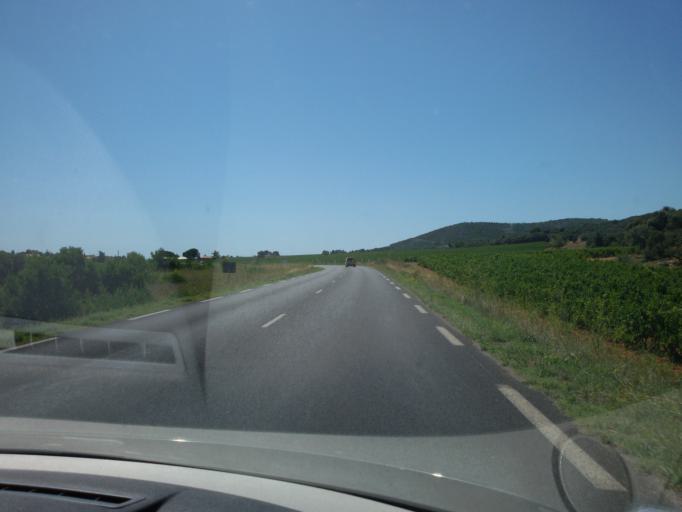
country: FR
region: Languedoc-Roussillon
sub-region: Departement de l'Herault
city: Vic-la-Gardiole
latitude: 43.4897
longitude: 3.7733
